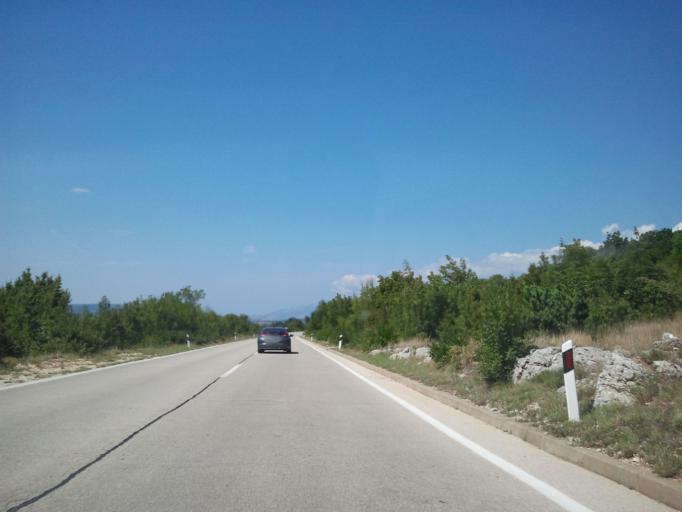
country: HR
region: Zadarska
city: Krusevo
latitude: 44.1724
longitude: 15.6212
